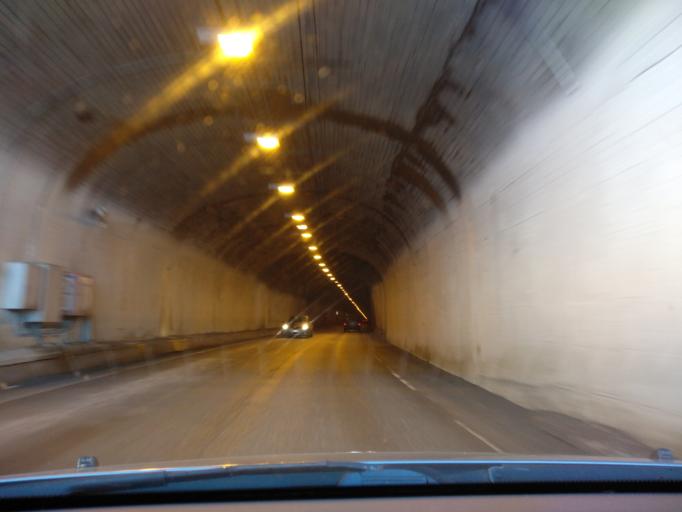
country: NO
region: Hordaland
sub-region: Odda
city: Odda
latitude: 59.8597
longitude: 6.6981
